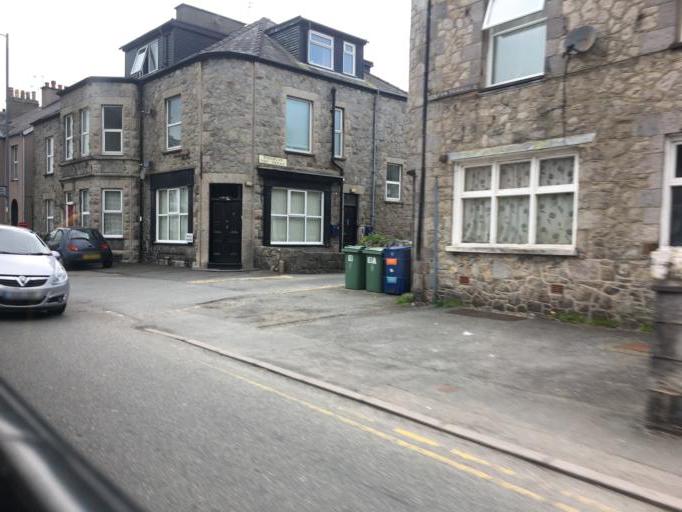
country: GB
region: Wales
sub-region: Gwynedd
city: Y Felinheli
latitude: 53.1863
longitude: -4.2068
